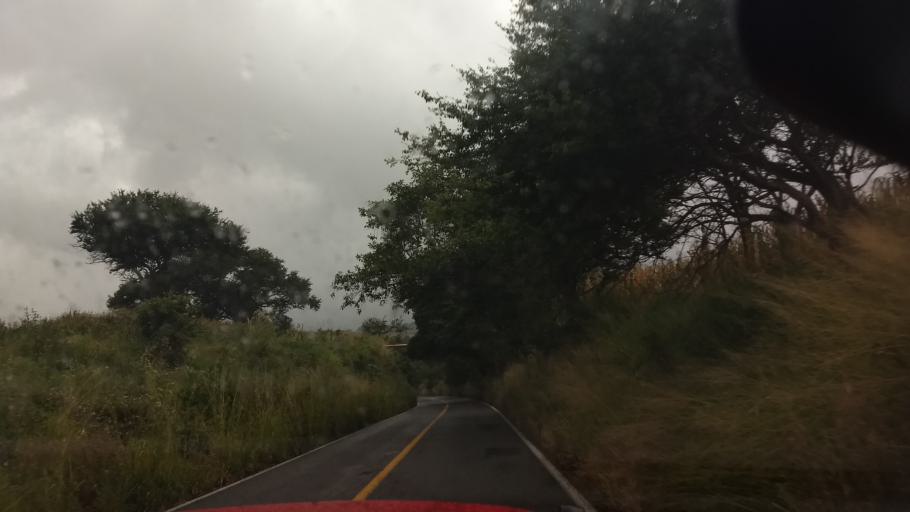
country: MX
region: Jalisco
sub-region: Tonila
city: San Marcos
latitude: 19.4386
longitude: -103.4921
